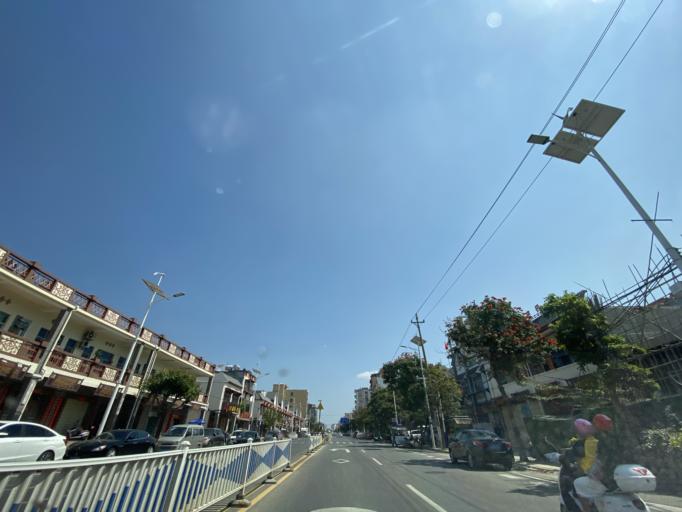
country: CN
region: Hainan
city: Yingzhou
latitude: 18.4221
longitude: 109.8481
